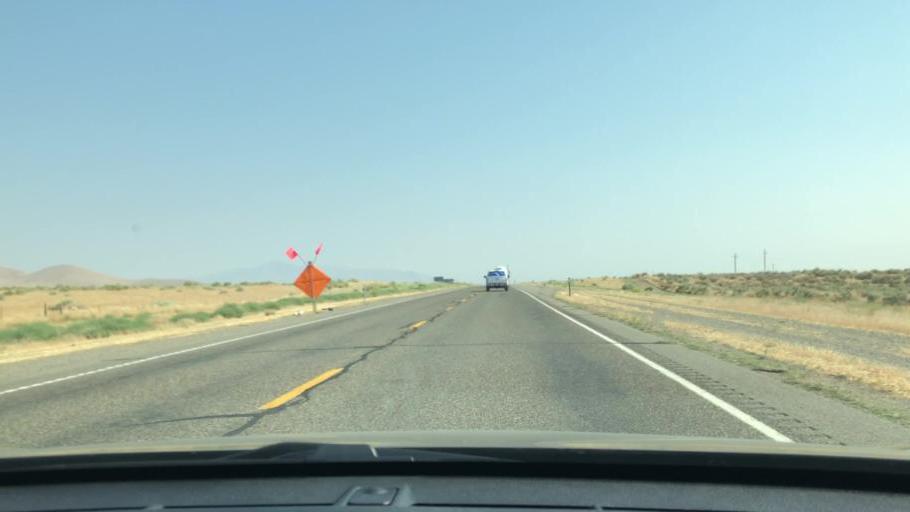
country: US
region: Nevada
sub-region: Humboldt County
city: Winnemucca
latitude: 41.1467
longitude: -117.6882
